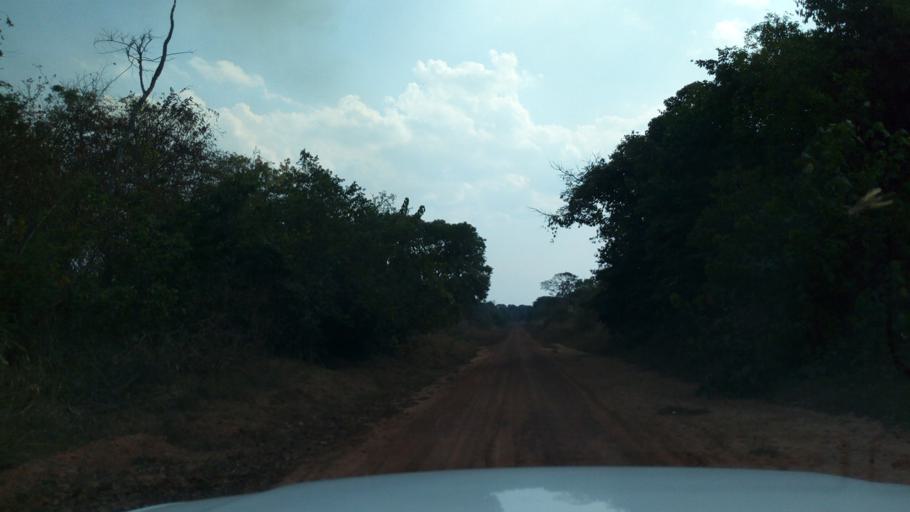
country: CD
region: Katanga
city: Kalemie
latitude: -5.4413
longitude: 28.9523
